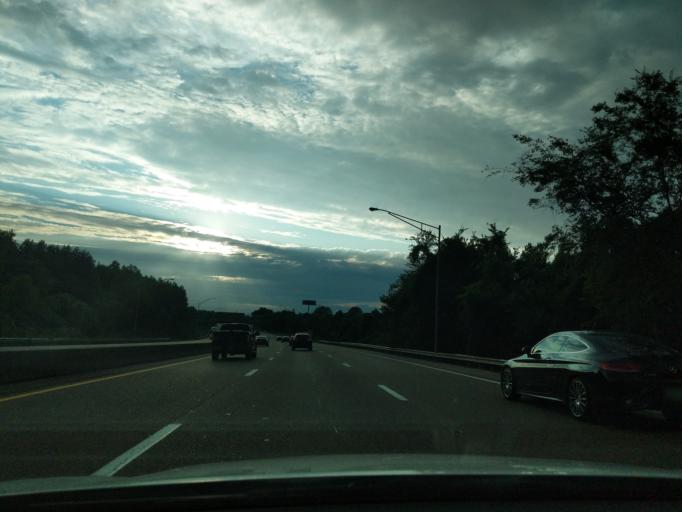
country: US
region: Tennessee
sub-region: Shelby County
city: New South Memphis
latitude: 35.0775
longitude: -90.0475
